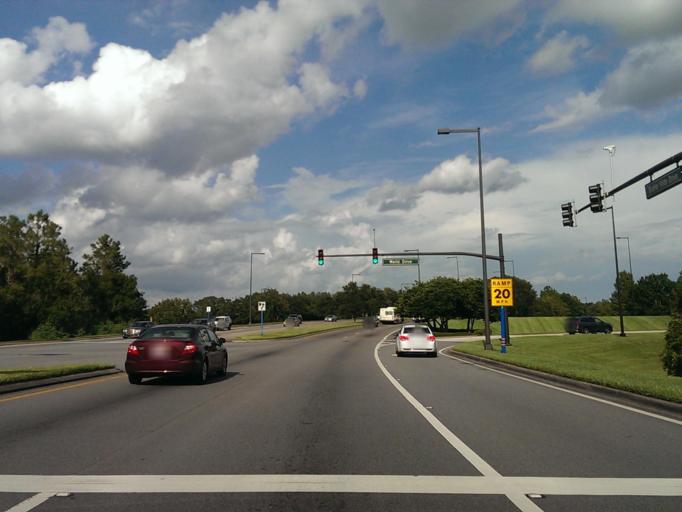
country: US
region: Florida
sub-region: Osceola County
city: Celebration
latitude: 28.3633
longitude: -81.5672
